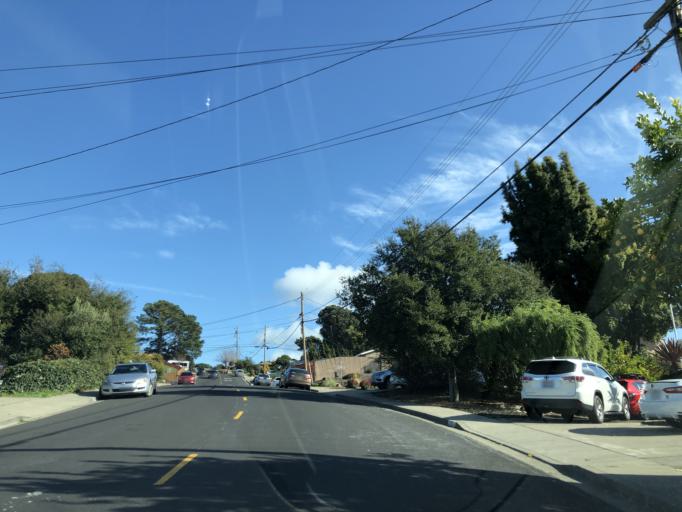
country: US
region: California
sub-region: Contra Costa County
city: Tara Hills
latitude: 37.9919
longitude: -122.3149
